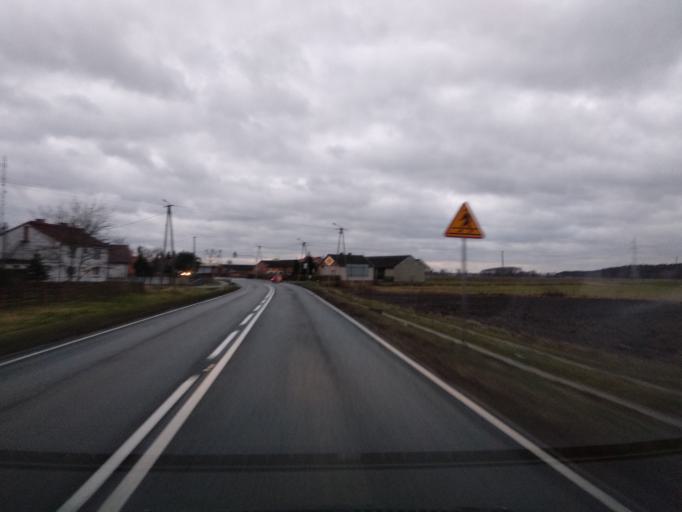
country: PL
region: Greater Poland Voivodeship
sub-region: Powiat koninski
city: Rychwal
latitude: 52.1235
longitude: 18.1717
